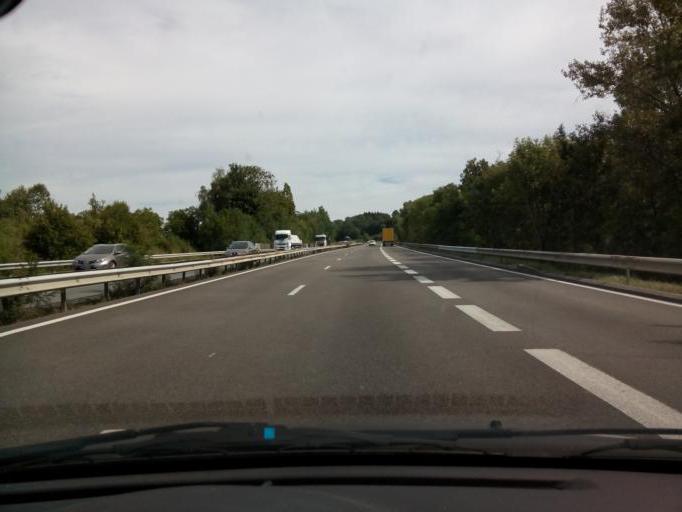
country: FR
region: Rhone-Alpes
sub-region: Departement de l'Isere
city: Saint-Victor-de-Cessieu
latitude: 45.5412
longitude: 5.3885
